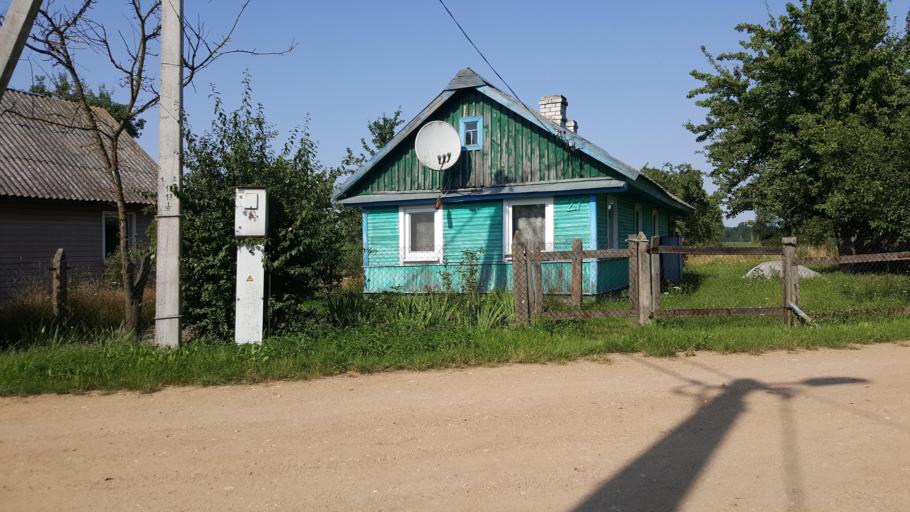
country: BY
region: Brest
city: Zhabinka
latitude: 52.2276
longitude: 23.9921
